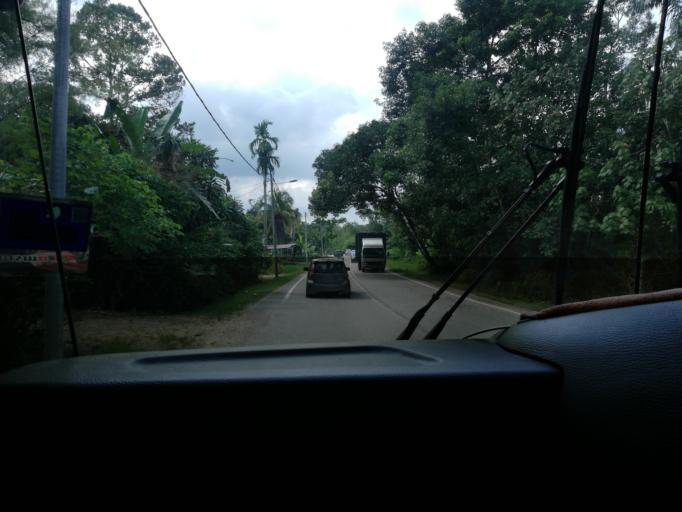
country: MY
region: Kedah
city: Kulim
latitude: 5.2969
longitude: 100.6236
